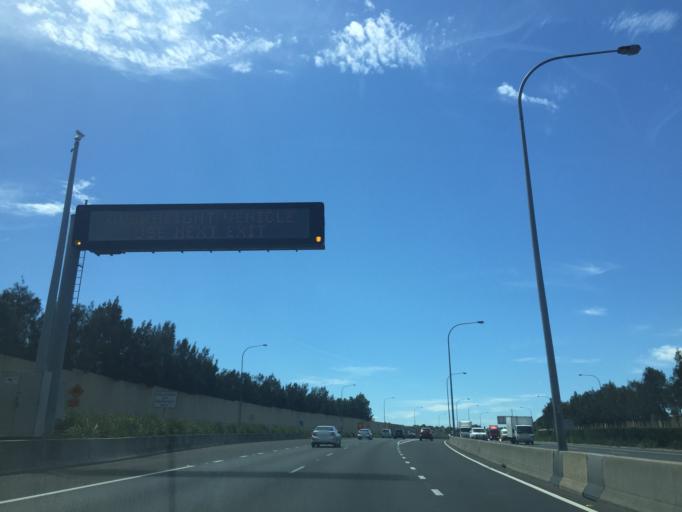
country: AU
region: New South Wales
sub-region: Rockdale
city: Bexley North
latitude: -33.9374
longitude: 151.1032
